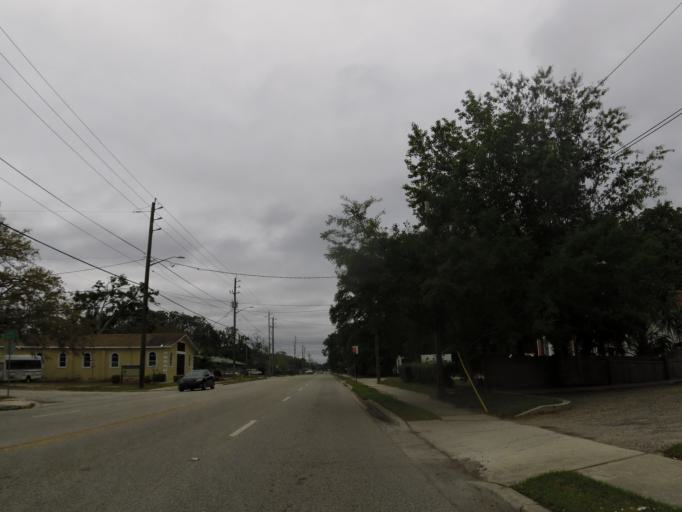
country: US
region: Florida
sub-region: Duval County
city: Jacksonville
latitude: 30.2814
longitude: -81.6437
